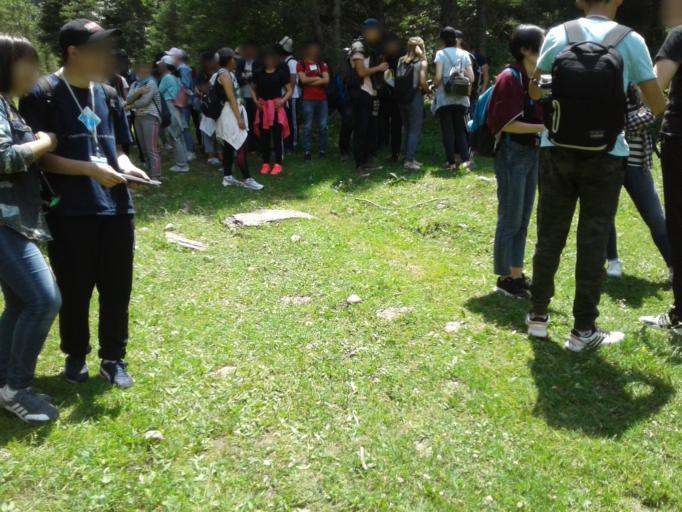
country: KG
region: Naryn
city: Naryn
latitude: 41.4173
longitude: 76.1862
